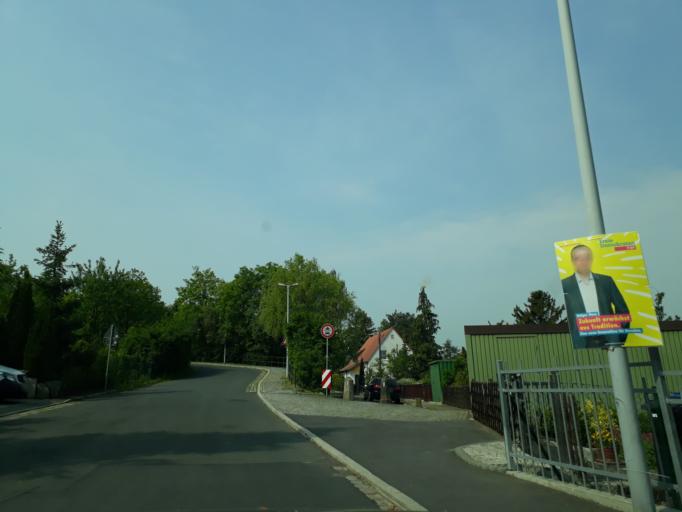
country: DE
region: Saxony
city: Bannewitz
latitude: 51.0111
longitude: 13.7498
